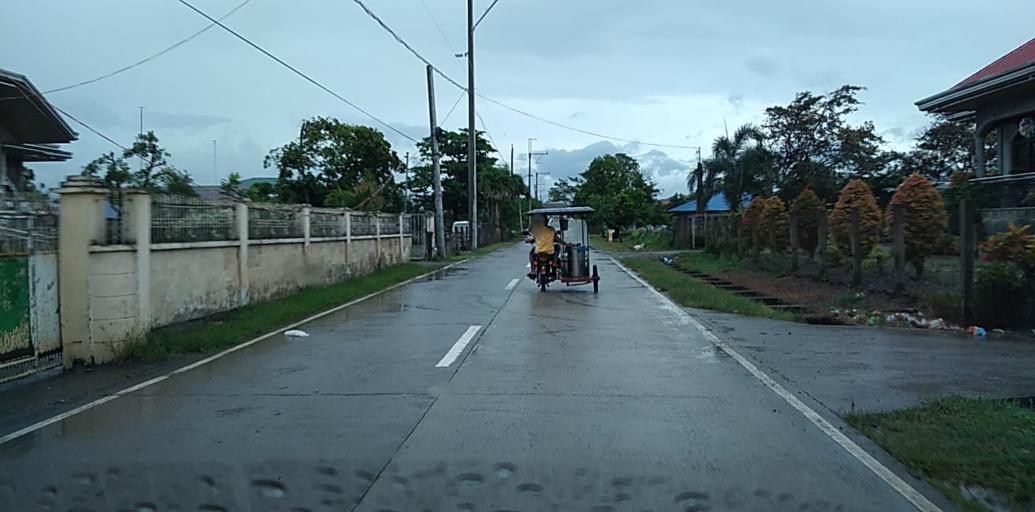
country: PH
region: Central Luzon
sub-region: Province of Pampanga
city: Salapungan
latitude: 15.1345
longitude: 120.9224
